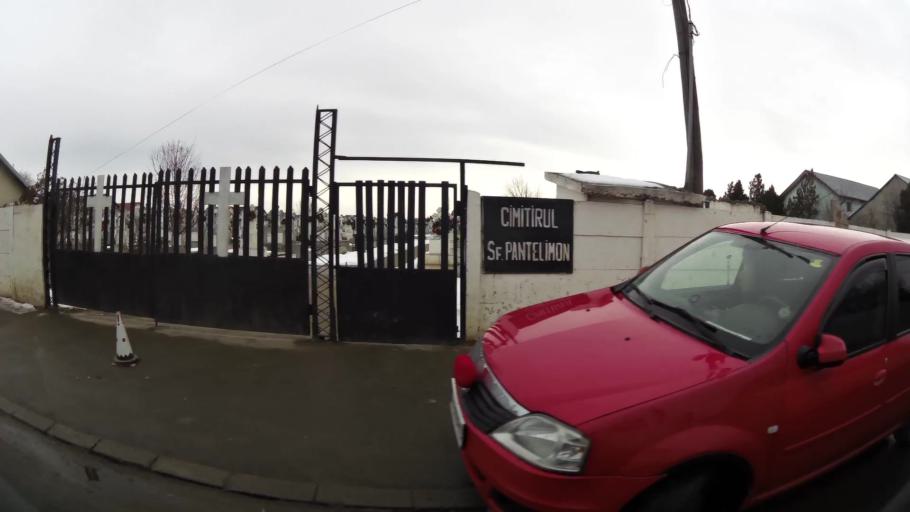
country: RO
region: Ilfov
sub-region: Comuna Pantelimon
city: Pantelimon
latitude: 44.4586
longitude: 26.2161
